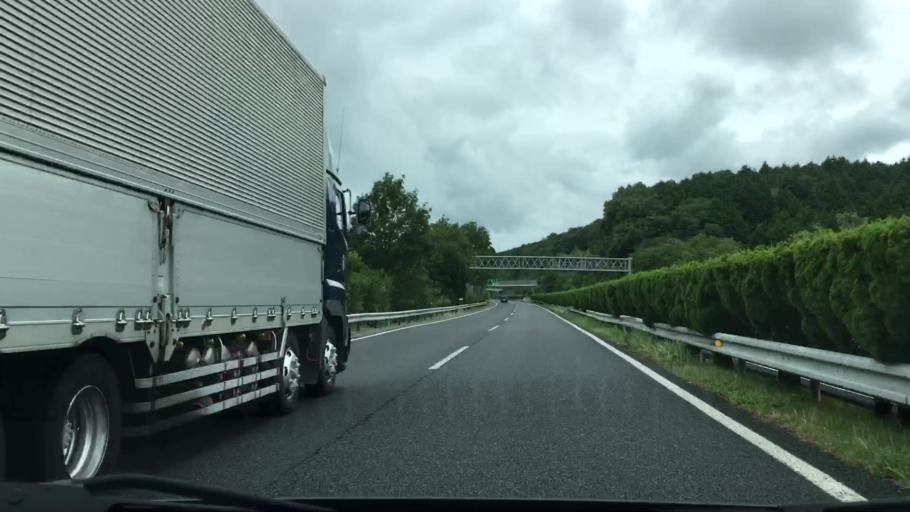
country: JP
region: Okayama
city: Tsuyama
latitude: 35.0381
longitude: 134.1301
